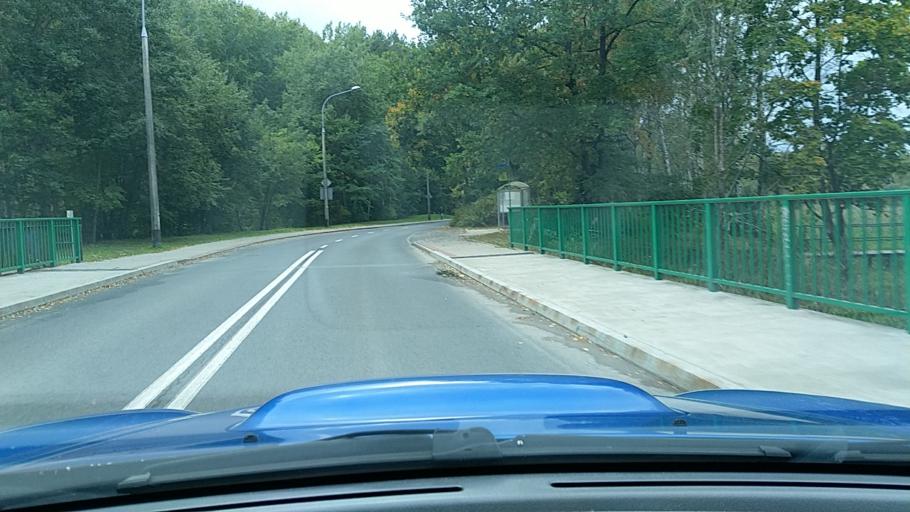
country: PL
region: Warmian-Masurian Voivodeship
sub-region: Olsztyn
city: Kortowo
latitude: 53.7454
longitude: 20.4680
